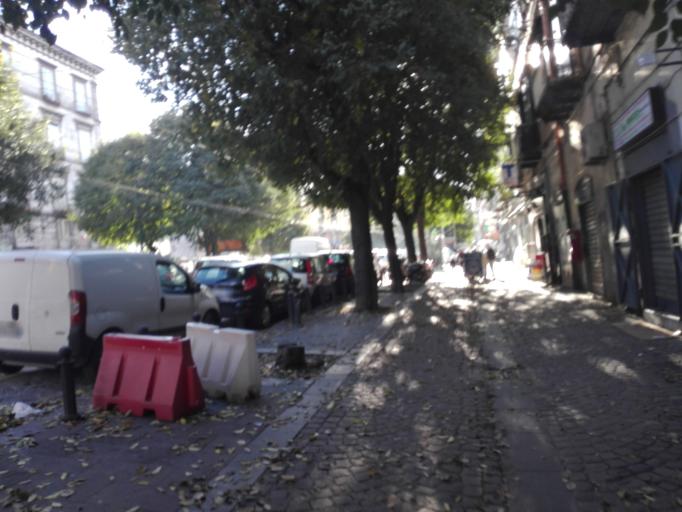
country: IT
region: Campania
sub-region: Provincia di Napoli
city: Napoli
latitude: 40.8579
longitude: 14.2605
